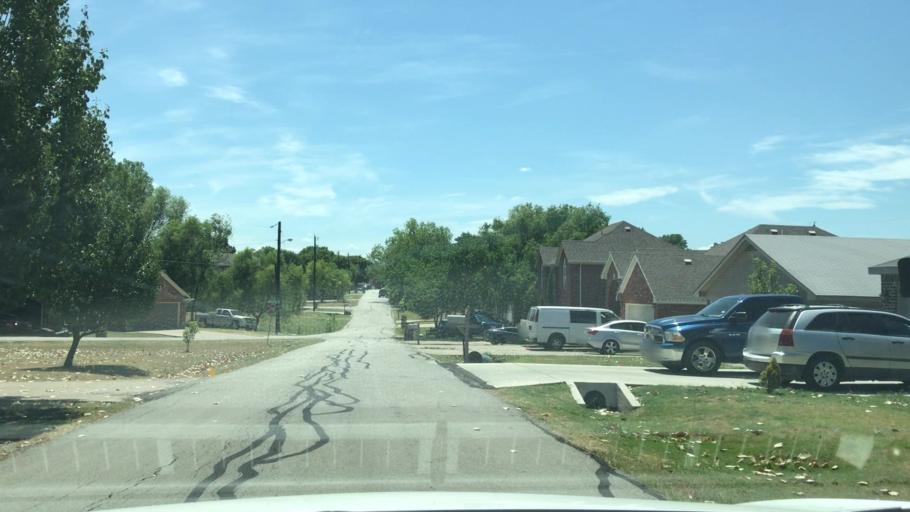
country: US
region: Texas
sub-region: Rockwall County
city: Rockwall
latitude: 32.8878
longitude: -96.4552
